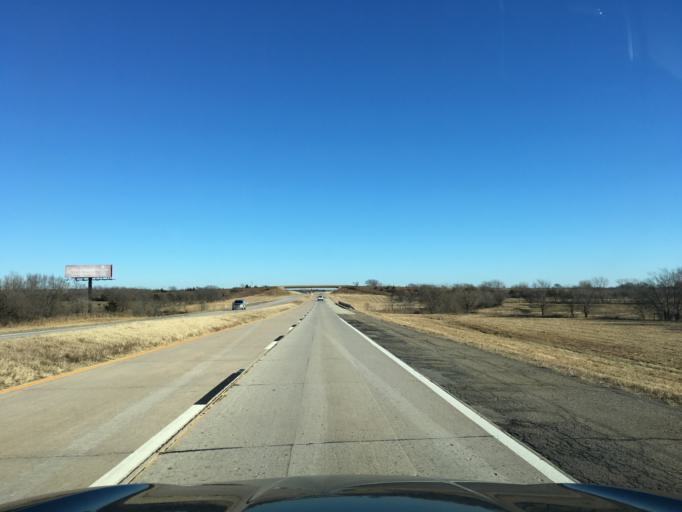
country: US
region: Oklahoma
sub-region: Payne County
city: Yale
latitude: 36.2245
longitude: -96.7186
